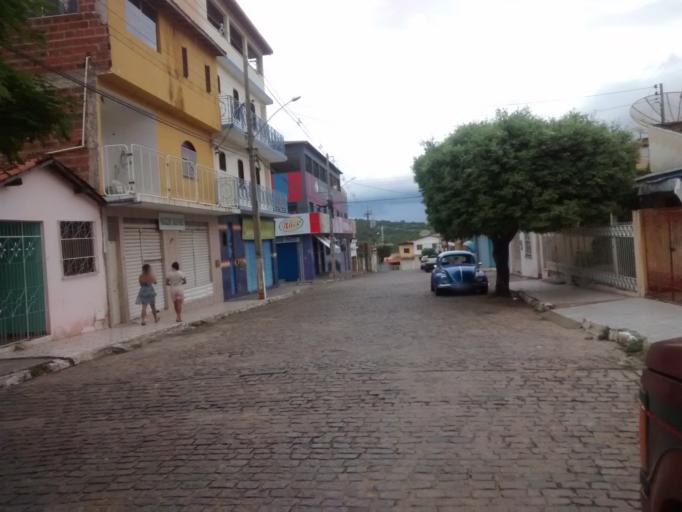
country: BR
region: Bahia
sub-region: Brumado
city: Brumado
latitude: -14.2096
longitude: -41.6733
